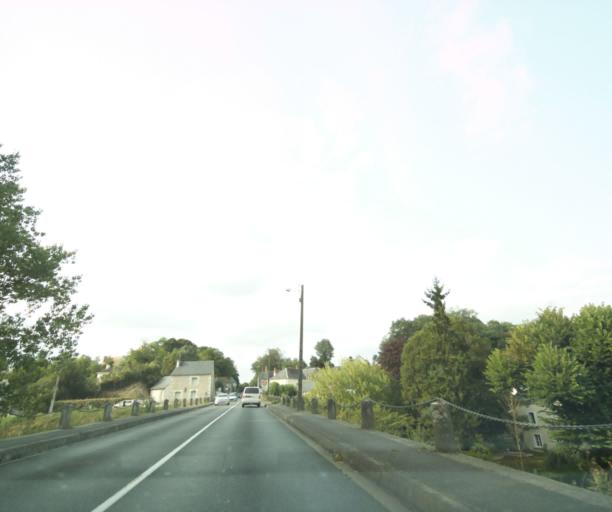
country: FR
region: Centre
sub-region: Departement d'Indre-et-Loire
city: Cormery
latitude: 47.2713
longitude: 0.8340
